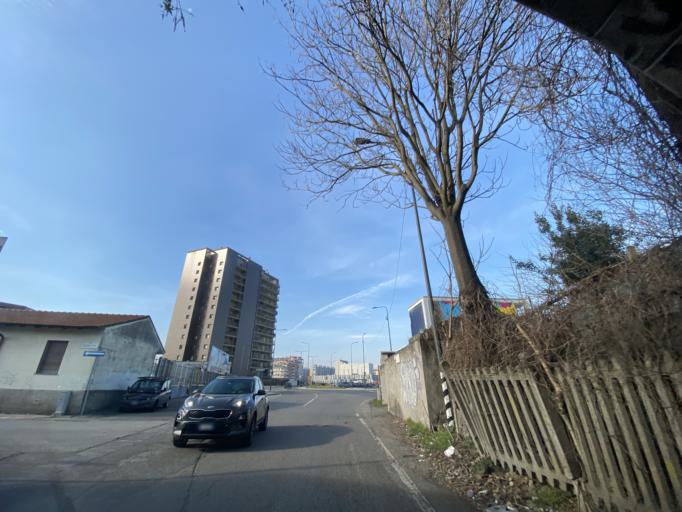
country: IT
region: Lombardy
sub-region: Citta metropolitana di Milano
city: Novate Milanese
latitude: 45.5085
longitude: 9.1489
